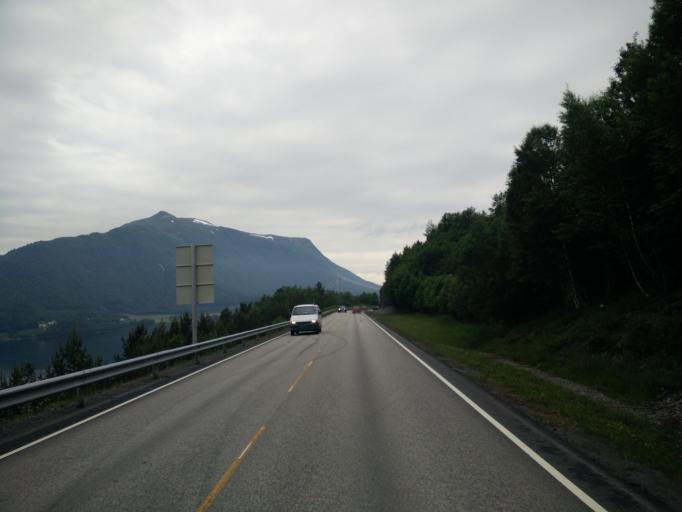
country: NO
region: More og Romsdal
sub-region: Kristiansund
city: Rensvik
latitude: 62.9714
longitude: 7.8019
